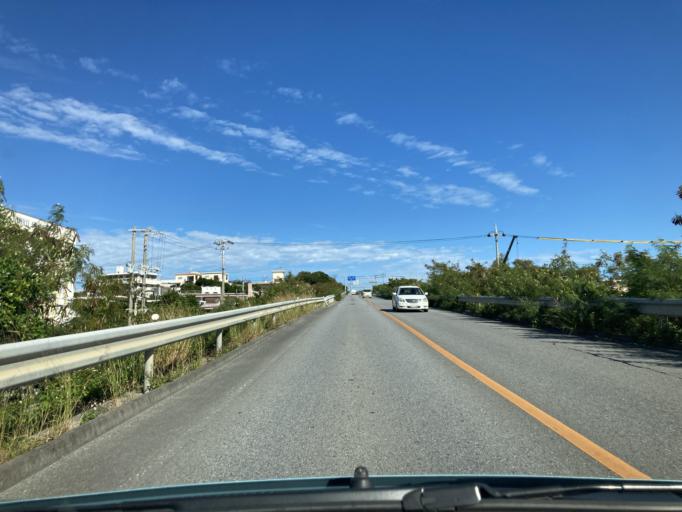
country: JP
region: Okinawa
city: Okinawa
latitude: 26.3800
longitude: 127.7455
